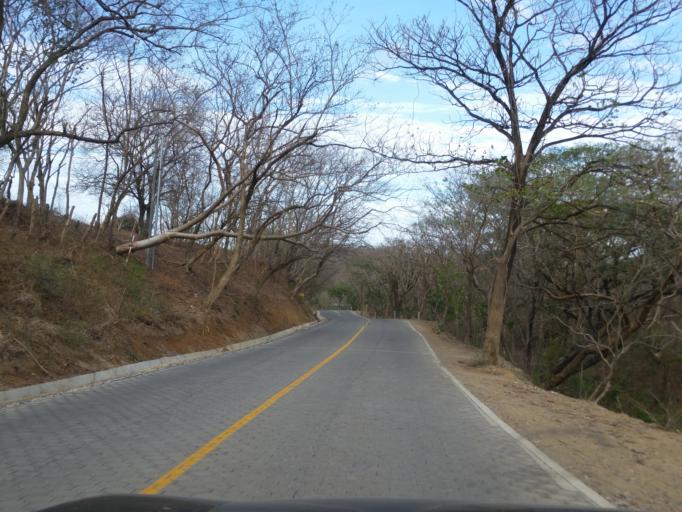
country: NI
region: Rivas
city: Tola
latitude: 11.3913
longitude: -85.9841
